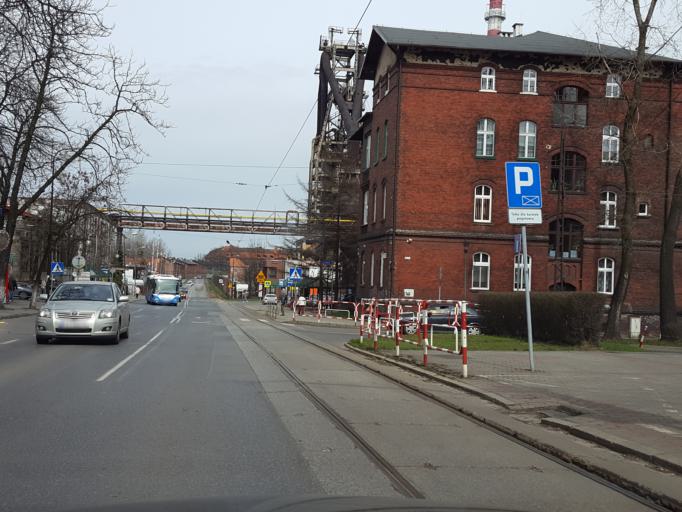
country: PL
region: Silesian Voivodeship
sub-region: Ruda Slaska
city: Ruda Slaska
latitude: 50.2884
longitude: 18.8752
